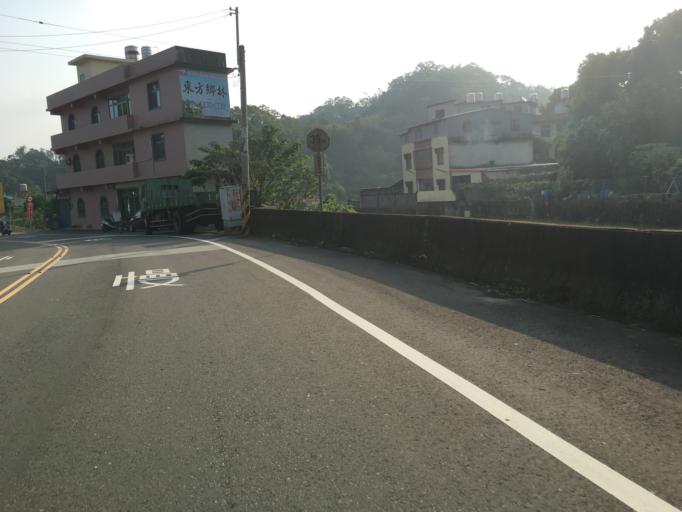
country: TW
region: Taiwan
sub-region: Hsinchu
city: Hsinchu
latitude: 24.7078
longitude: 121.0454
